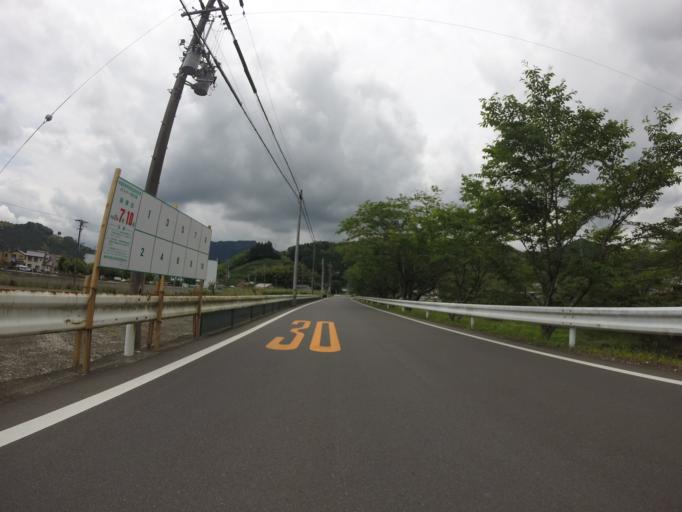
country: JP
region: Shizuoka
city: Shizuoka-shi
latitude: 34.9883
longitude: 138.3087
